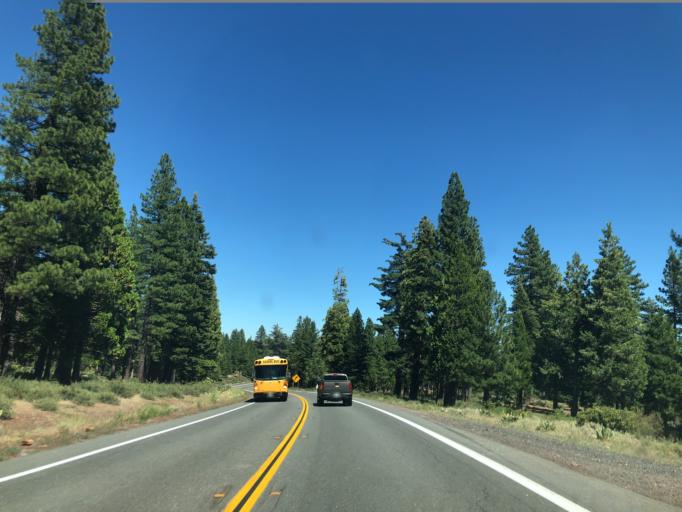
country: US
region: California
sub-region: Lassen County
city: Susanville
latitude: 40.4260
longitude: -120.8100
